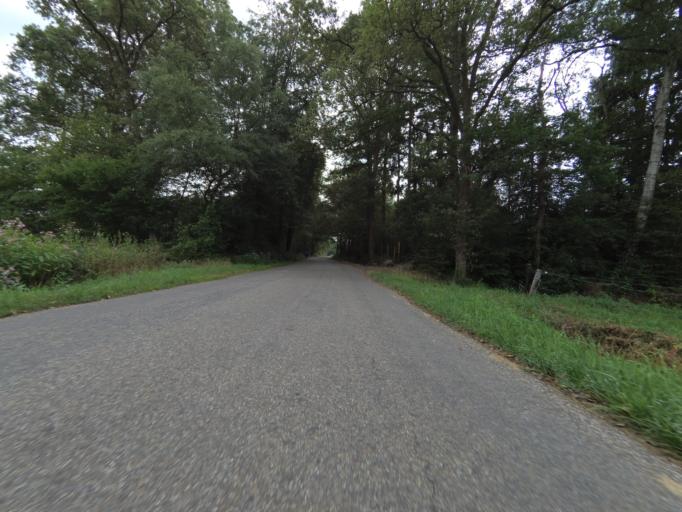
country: NL
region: Overijssel
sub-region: Gemeente Hengelo
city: Hengelo
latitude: 52.2571
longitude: 6.8404
